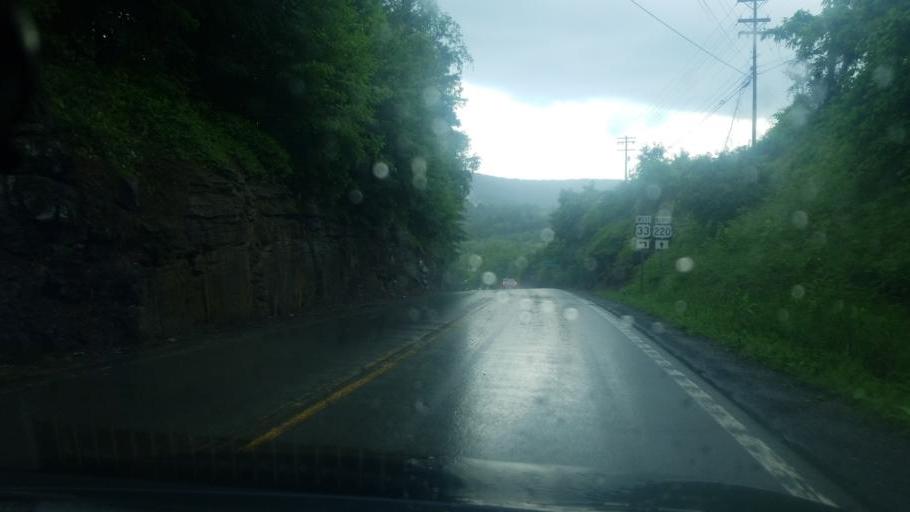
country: US
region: West Virginia
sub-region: Pendleton County
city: Franklin
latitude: 38.6527
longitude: -79.3306
